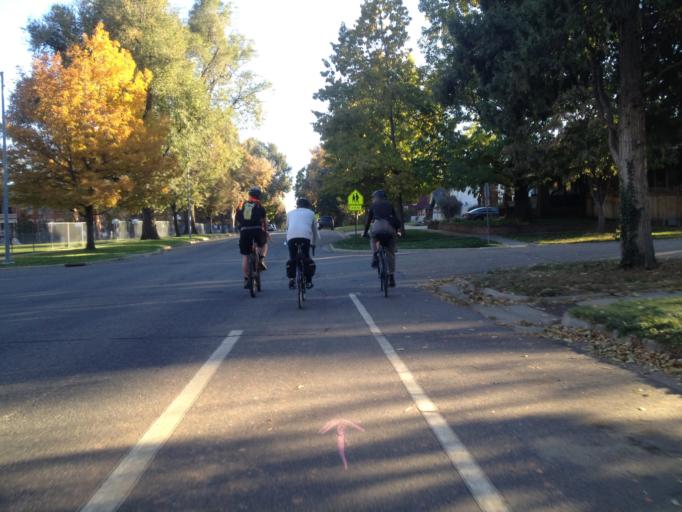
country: US
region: Colorado
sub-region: Boulder County
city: Longmont
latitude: 40.1675
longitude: -105.1103
